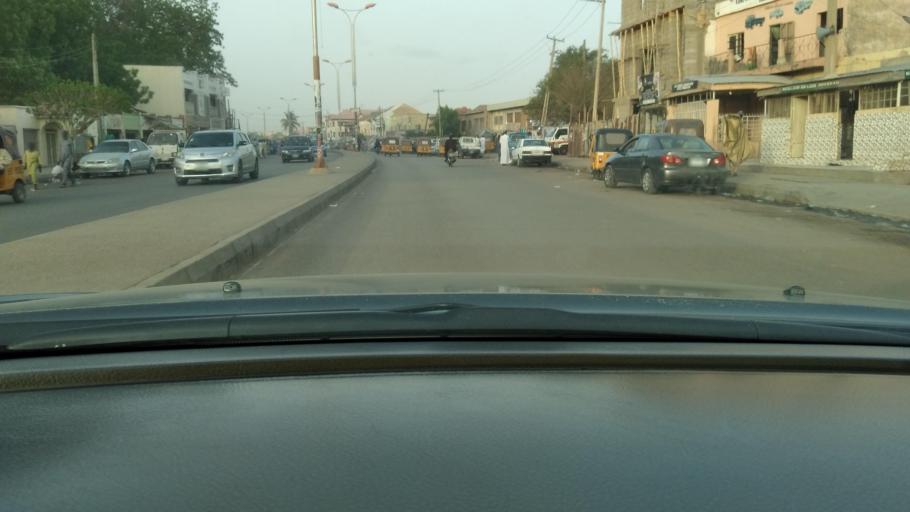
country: NG
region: Kano
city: Kano
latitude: 11.9641
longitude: 8.5268
